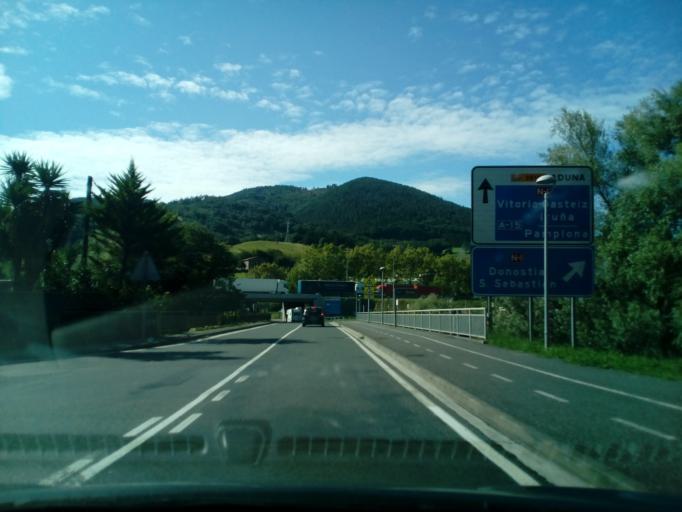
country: ES
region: Basque Country
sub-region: Provincia de Guipuzcoa
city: Andoain
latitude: 43.2086
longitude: -2.0330
